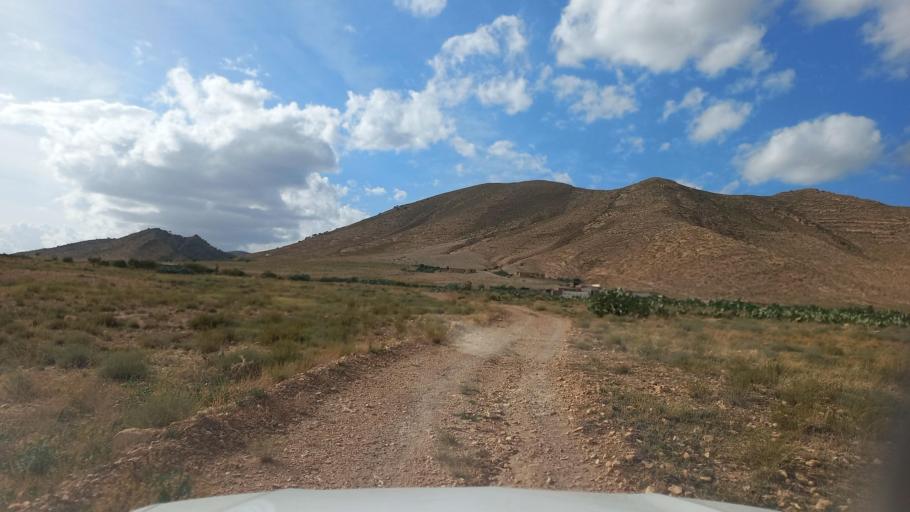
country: TN
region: Al Qasrayn
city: Sbiba
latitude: 35.4551
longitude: 9.0710
